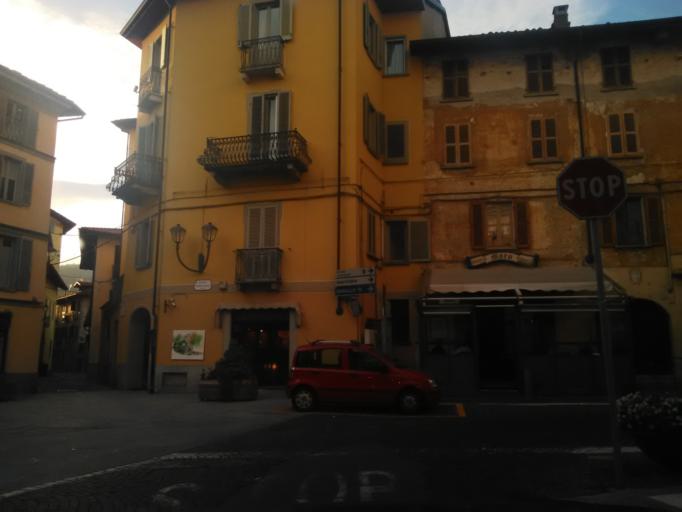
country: IT
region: Piedmont
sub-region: Provincia di Vercelli
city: Borgosesia
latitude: 45.7164
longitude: 8.2759
